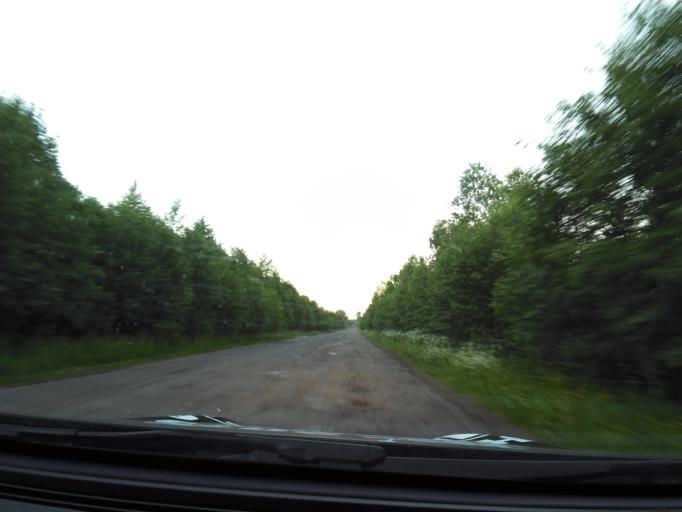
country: RU
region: Leningrad
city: Voznesen'ye
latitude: 60.8268
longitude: 35.7165
